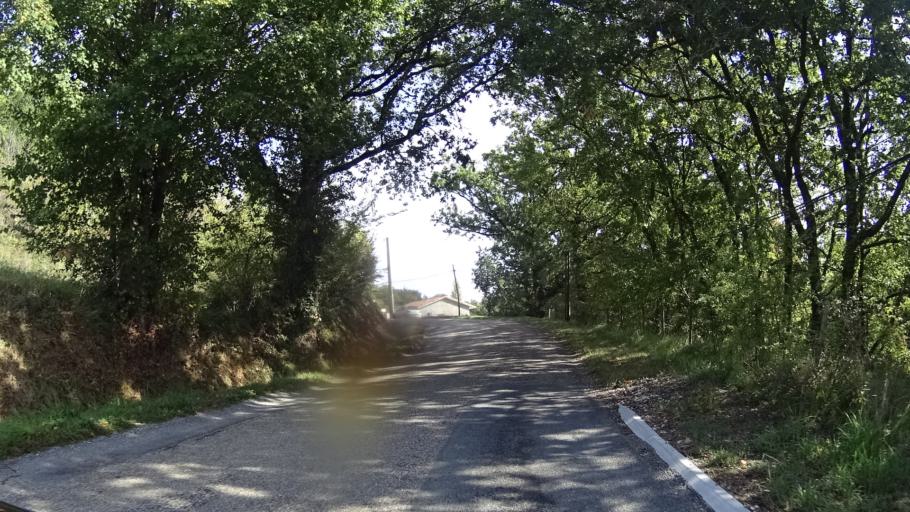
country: FR
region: Aquitaine
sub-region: Departement du Lot-et-Garonne
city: Pont-du-Casse
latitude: 44.2154
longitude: 0.7449
